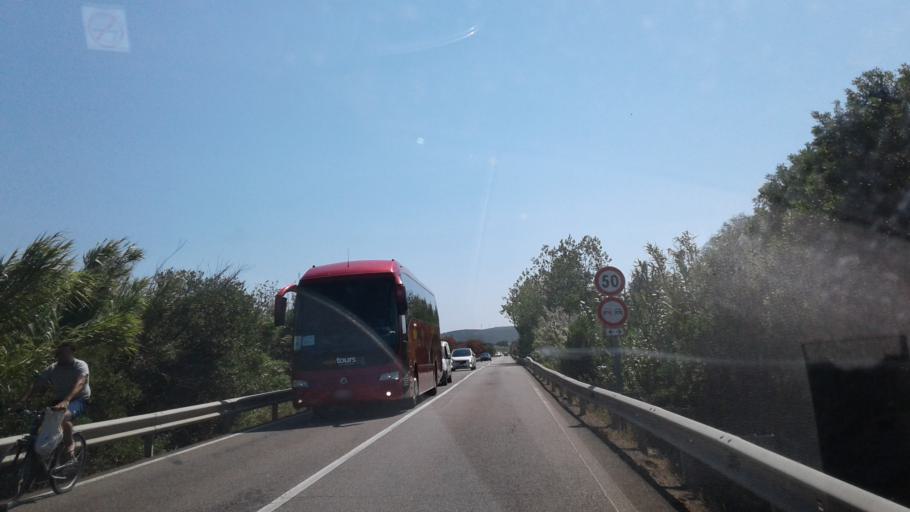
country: IT
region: Sardinia
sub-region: Provincia di Olbia-Tempio
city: Palau
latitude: 41.1711
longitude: 9.3463
